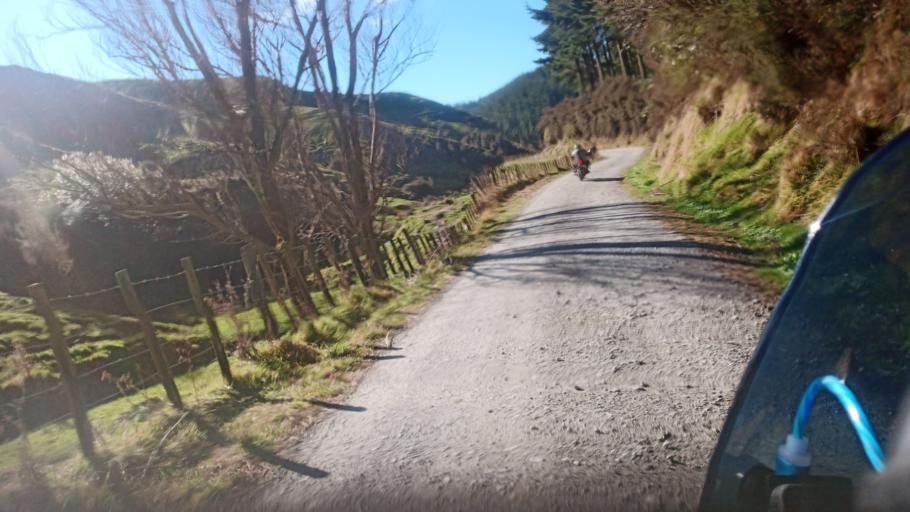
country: NZ
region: Hawke's Bay
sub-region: Wairoa District
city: Wairoa
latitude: -38.6596
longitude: 177.4888
